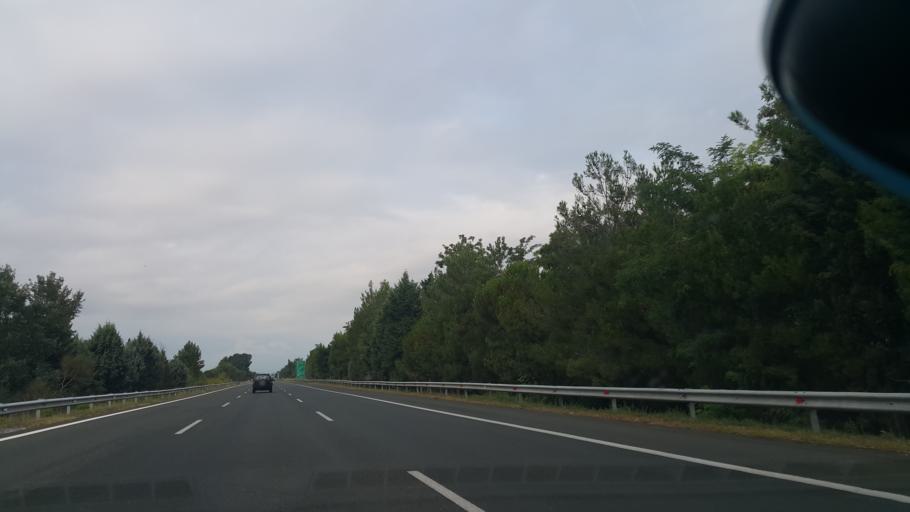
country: GR
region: Central Macedonia
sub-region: Nomos Pierias
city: Peristasi
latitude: 40.3006
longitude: 22.5489
